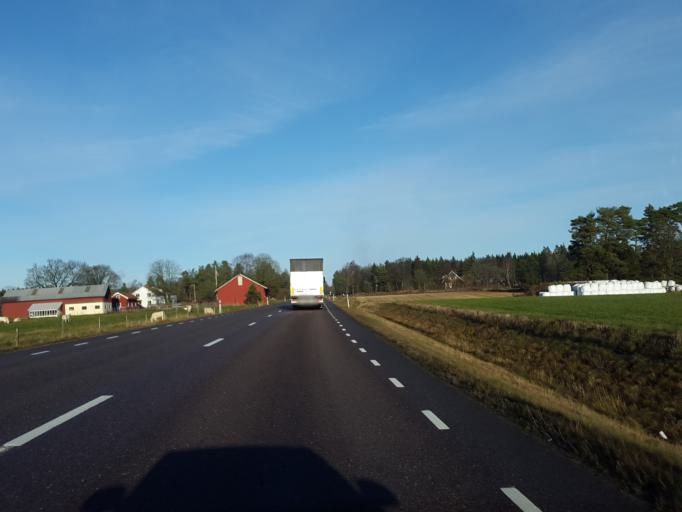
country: SE
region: Vaestra Goetaland
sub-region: Vargarda Kommun
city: Vargarda
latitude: 57.9997
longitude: 12.8110
